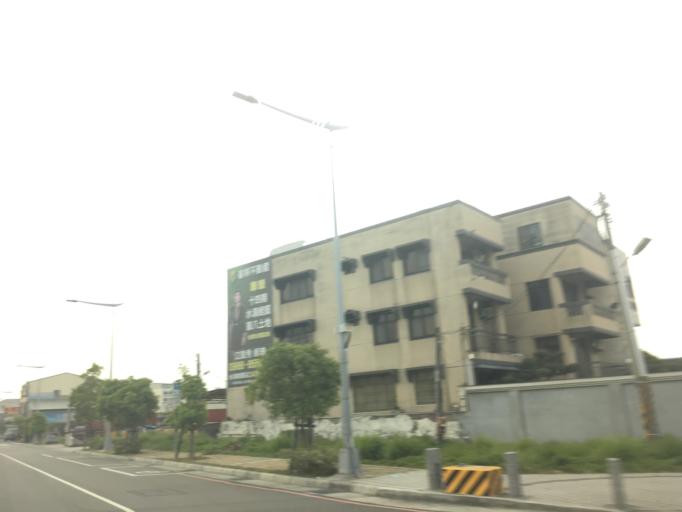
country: TW
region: Taiwan
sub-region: Taichung City
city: Taichung
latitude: 24.1934
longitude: 120.6737
